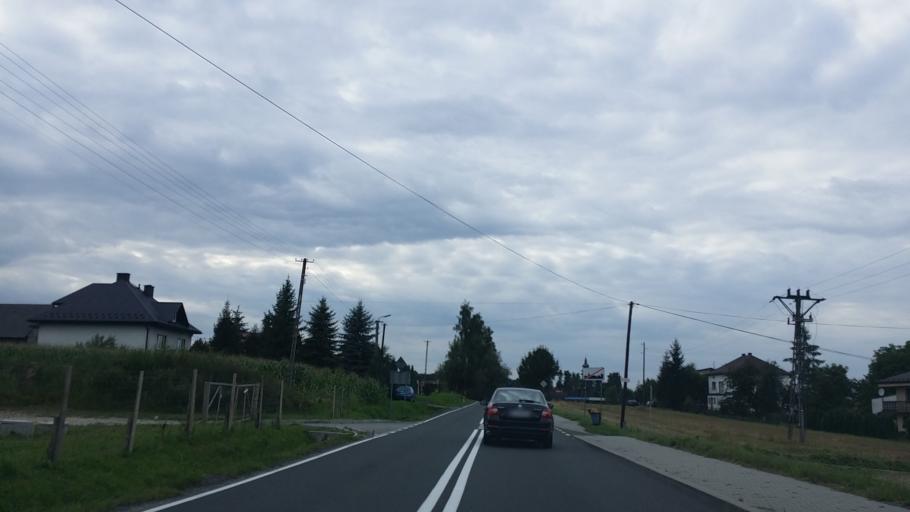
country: PL
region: Lesser Poland Voivodeship
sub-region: Powiat wadowicki
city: Ryczow
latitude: 49.9767
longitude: 19.5586
